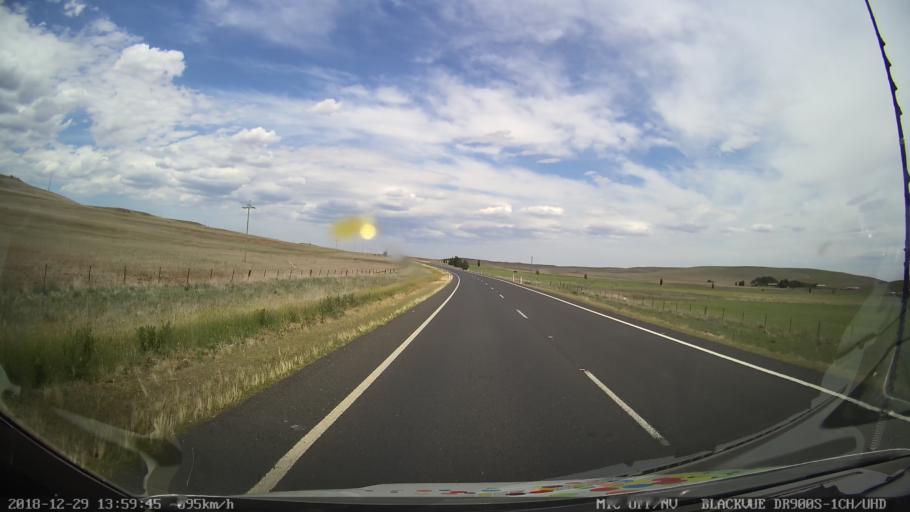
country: AU
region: New South Wales
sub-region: Cooma-Monaro
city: Cooma
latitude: -36.2568
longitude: 149.1508
